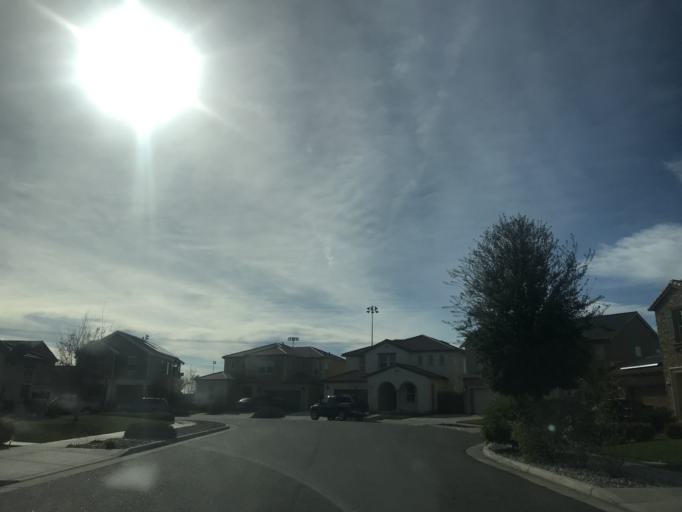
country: US
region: California
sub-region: Yolo County
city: Woodland
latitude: 38.6566
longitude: -121.7607
